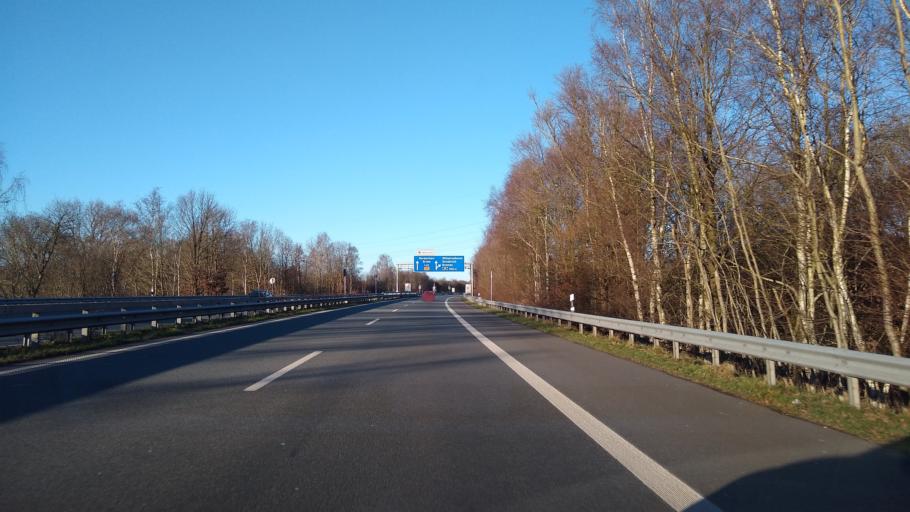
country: DE
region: Lower Saxony
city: Rastede
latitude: 53.1990
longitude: 8.2213
